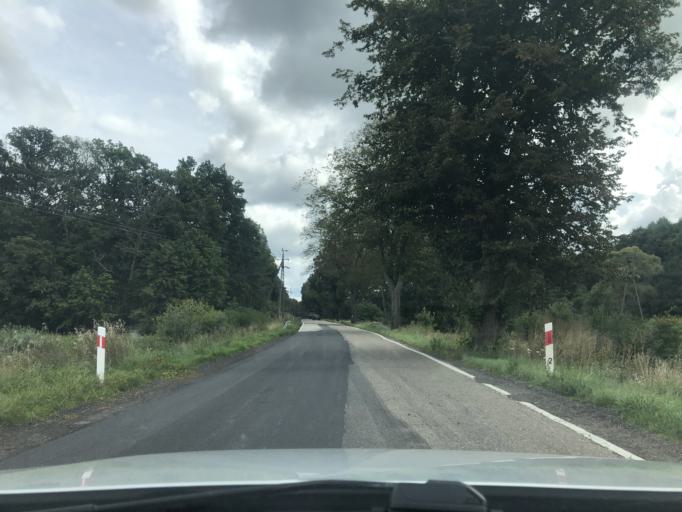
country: PL
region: Greater Poland Voivodeship
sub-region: Powiat czarnkowsko-trzcianecki
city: Wielen
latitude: 52.9043
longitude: 16.0963
